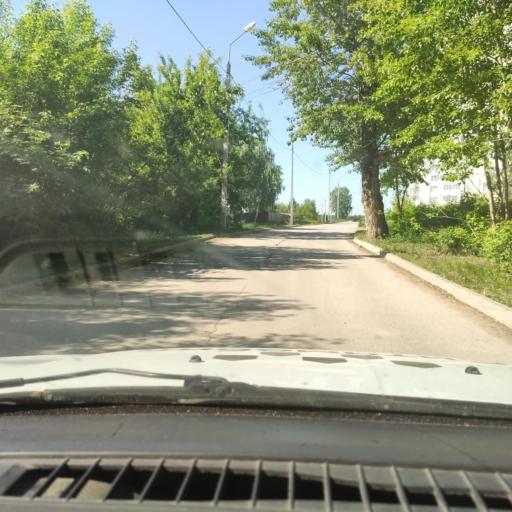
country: RU
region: Perm
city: Perm
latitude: 58.0972
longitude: 56.3010
